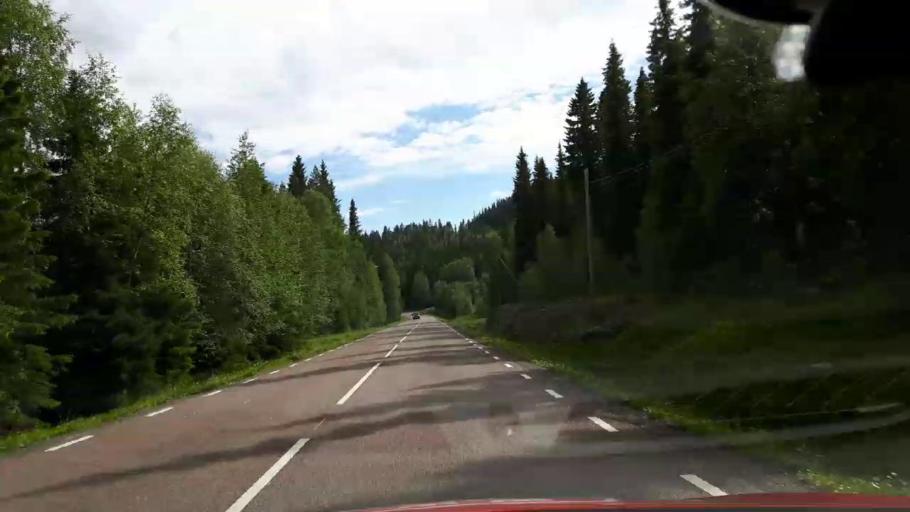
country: SE
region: Jaemtland
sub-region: Krokoms Kommun
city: Valla
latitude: 63.9207
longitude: 14.2142
